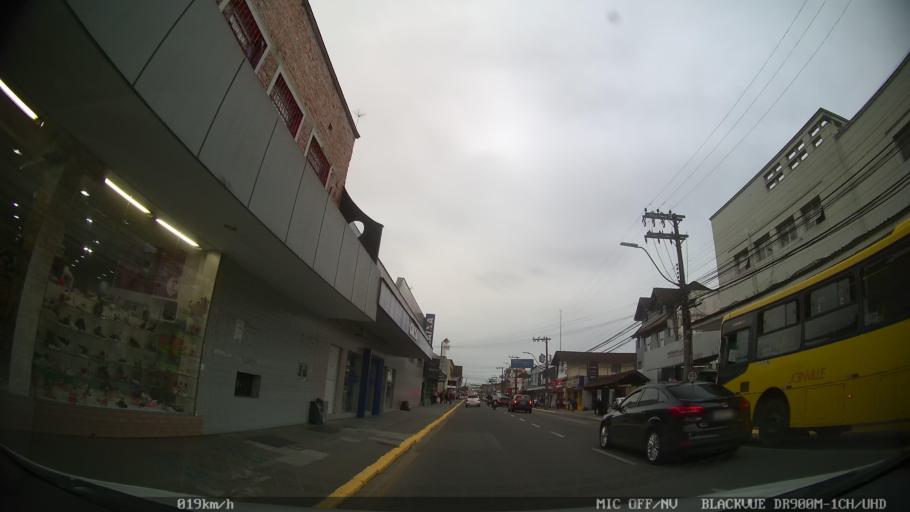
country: BR
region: Santa Catarina
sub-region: Joinville
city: Joinville
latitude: -26.2994
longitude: -48.8478
